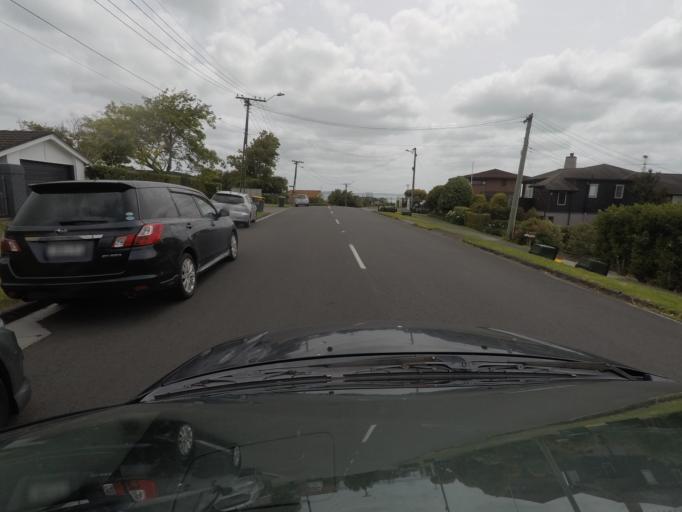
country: NZ
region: Auckland
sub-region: Auckland
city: Pakuranga
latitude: -36.8898
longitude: 174.9307
